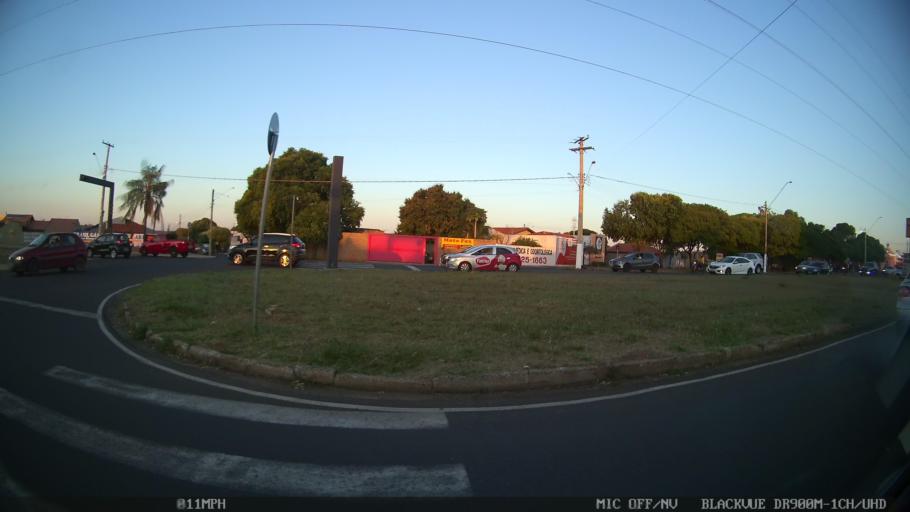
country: BR
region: Sao Paulo
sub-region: Sao Jose Do Rio Preto
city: Sao Jose do Rio Preto
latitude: -20.7937
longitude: -49.3449
